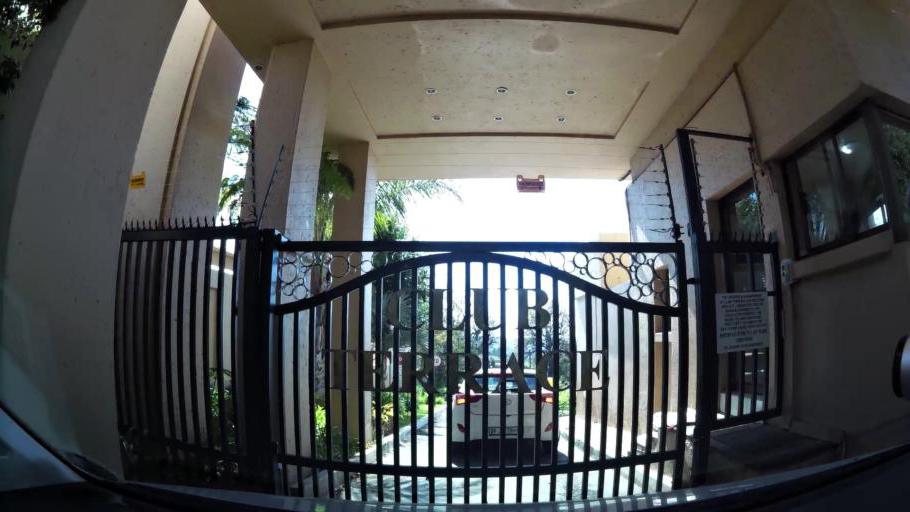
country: ZA
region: Gauteng
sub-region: City of Johannesburg Metropolitan Municipality
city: Johannesburg
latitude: -26.1644
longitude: 28.0957
